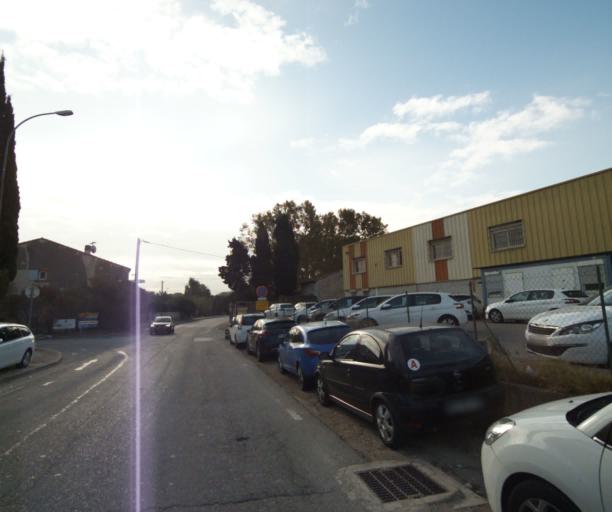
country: FR
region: Provence-Alpes-Cote d'Azur
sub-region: Departement des Bouches-du-Rhone
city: Saint-Victoret
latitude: 43.4224
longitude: 5.2428
